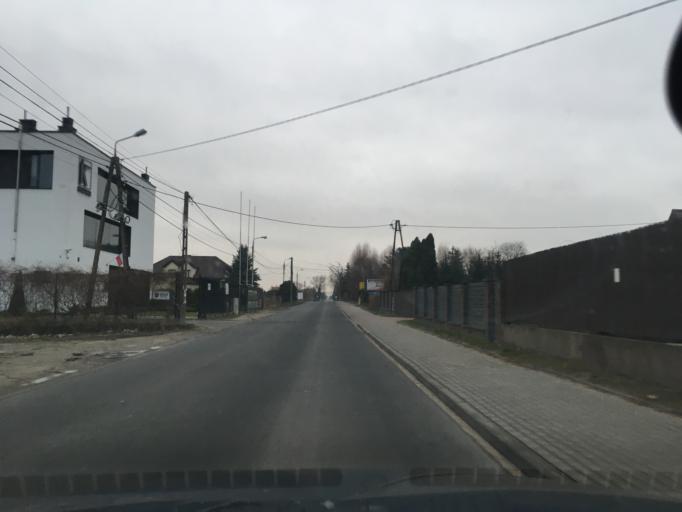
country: PL
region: Masovian Voivodeship
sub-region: Powiat piaseczynski
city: Mysiadlo
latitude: 52.1272
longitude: 20.9797
